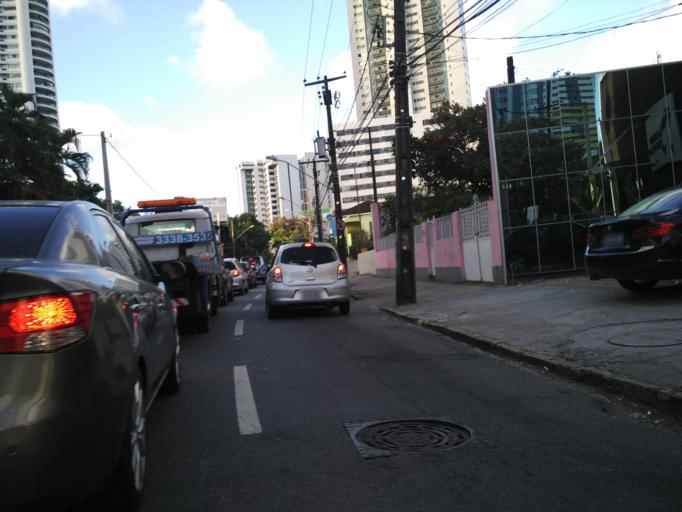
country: BR
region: Pernambuco
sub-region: Recife
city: Recife
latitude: -8.0468
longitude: -34.8971
